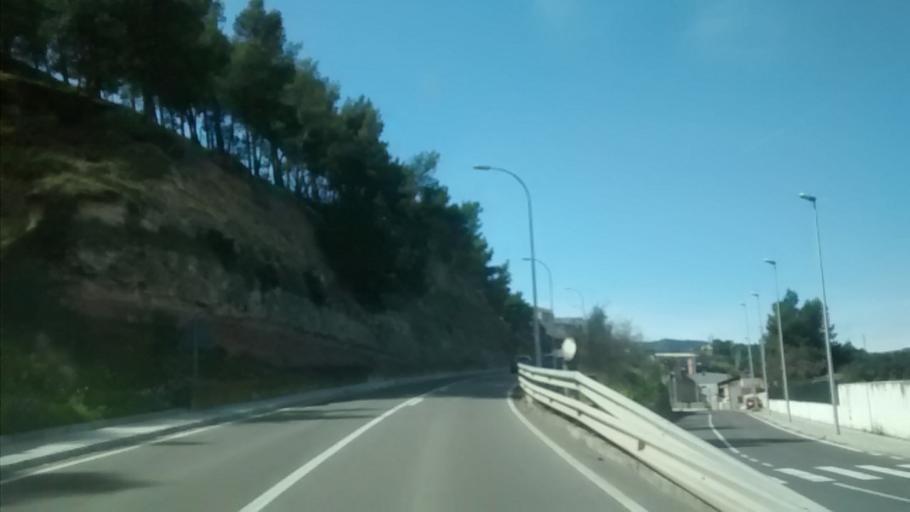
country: ES
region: Catalonia
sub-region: Provincia de Tarragona
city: Flix
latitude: 41.2305
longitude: 0.5468
